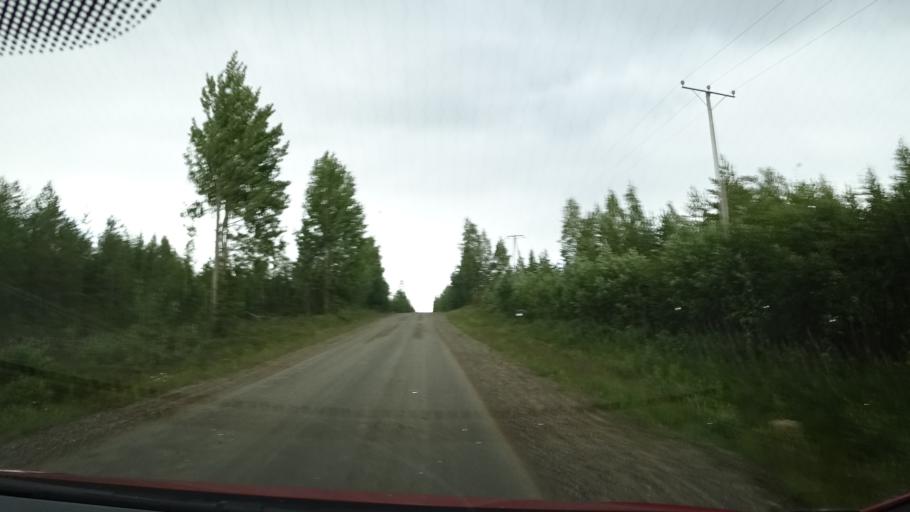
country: FI
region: Kainuu
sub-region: Kehys-Kainuu
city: Kuhmo
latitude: 63.9371
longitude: 29.2073
